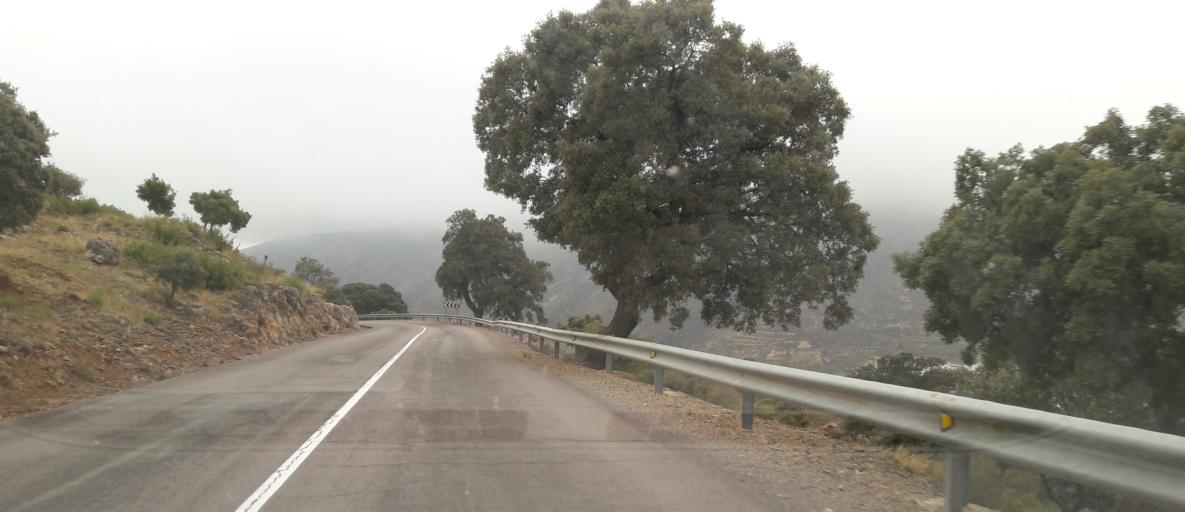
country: ES
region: Andalusia
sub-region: Provincia de Almeria
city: Enix
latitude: 36.8926
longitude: -2.6185
